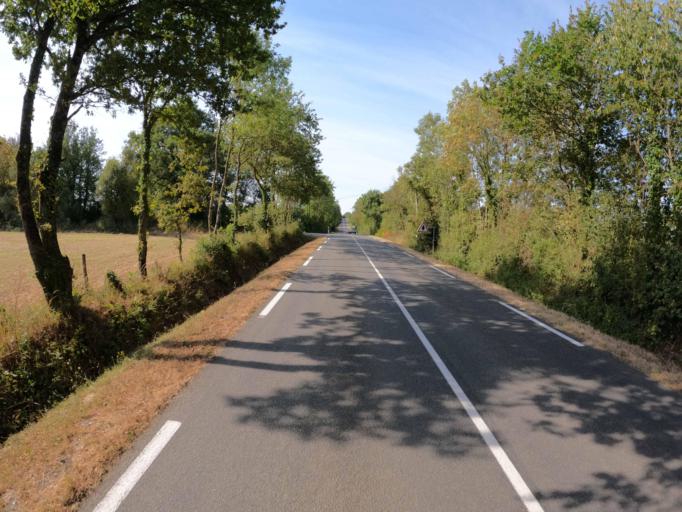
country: FR
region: Pays de la Loire
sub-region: Departement de la Vendee
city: Falleron
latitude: 46.8711
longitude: -1.7051
